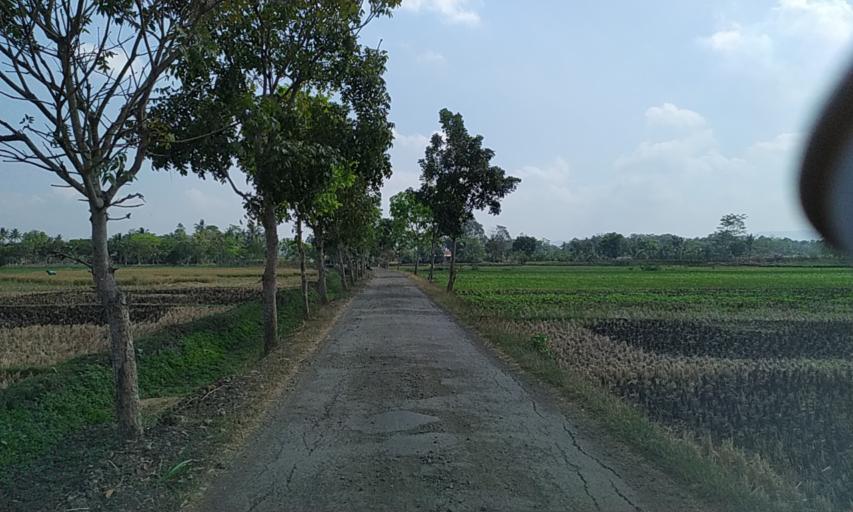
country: ID
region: Central Java
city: Tambaksari
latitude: -7.4919
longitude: 108.7590
